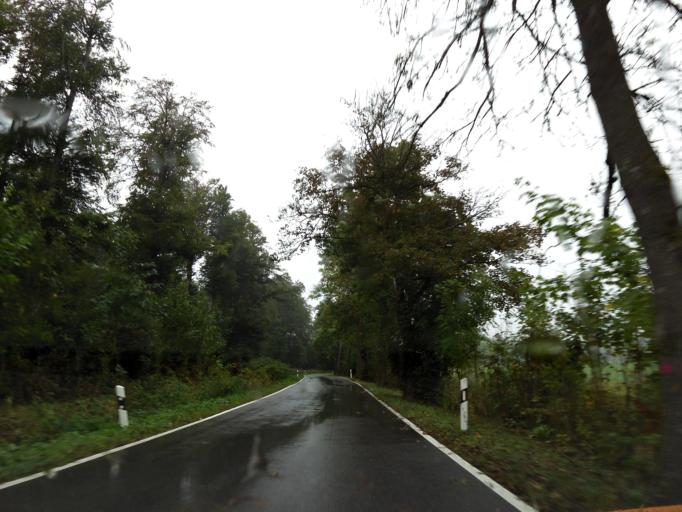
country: DE
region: Saxony-Anhalt
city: Hasselfelde
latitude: 51.6566
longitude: 10.8604
